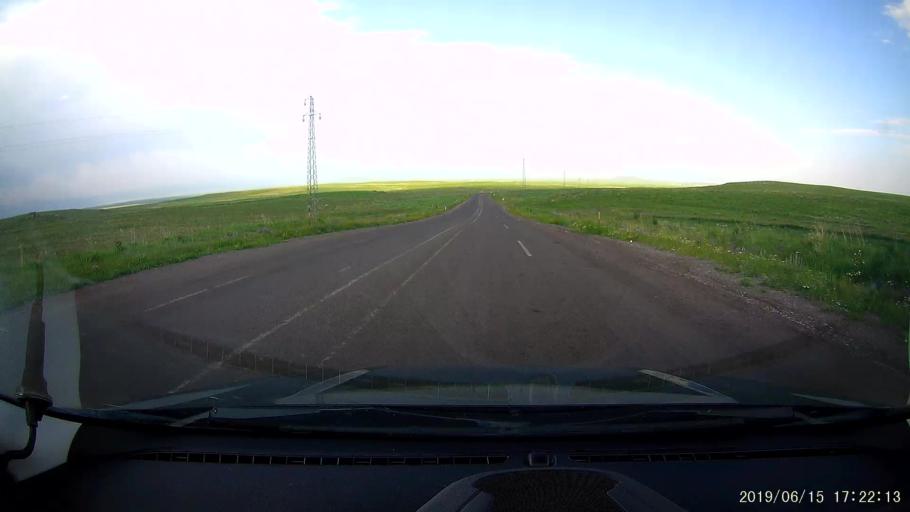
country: TR
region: Kars
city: Basgedikler
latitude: 40.6186
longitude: 43.3392
